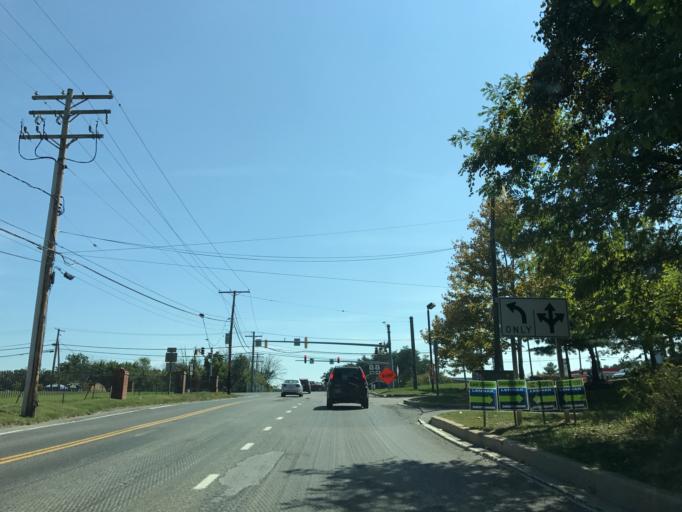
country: US
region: Maryland
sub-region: Anne Arundel County
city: Jessup
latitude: 39.1847
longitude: -76.7645
